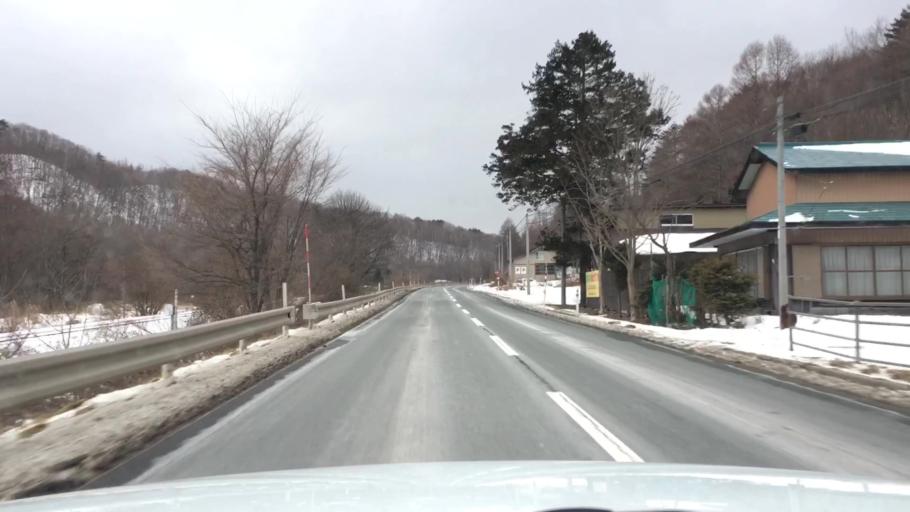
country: JP
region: Iwate
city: Morioka-shi
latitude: 39.6377
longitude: 141.4315
